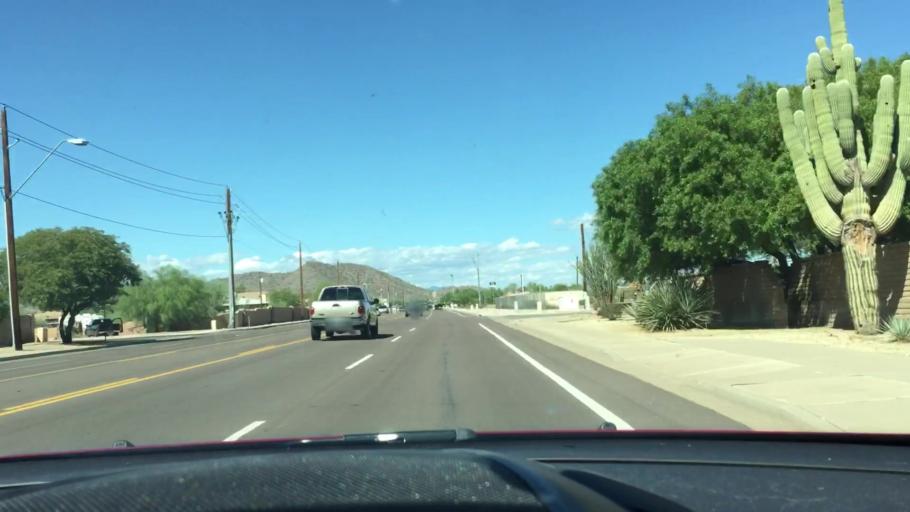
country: US
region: Arizona
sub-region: Maricopa County
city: Sun City
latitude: 33.6884
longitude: -112.2376
